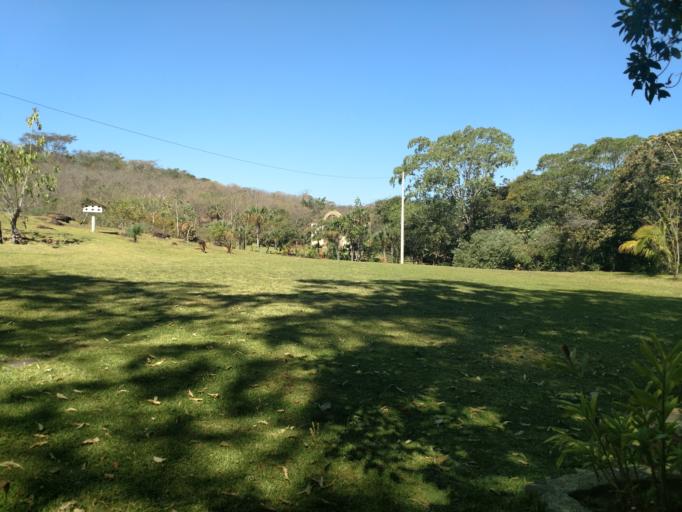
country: MX
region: Nayarit
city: Tepic
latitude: 21.5684
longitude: -104.9986
